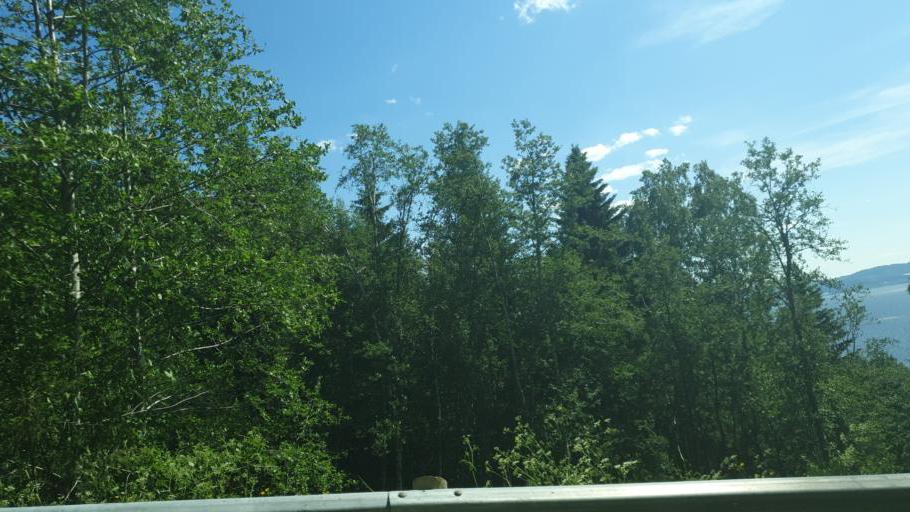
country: NO
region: Nord-Trondelag
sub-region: Frosta
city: Frosta
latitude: 63.7099
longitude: 10.7735
